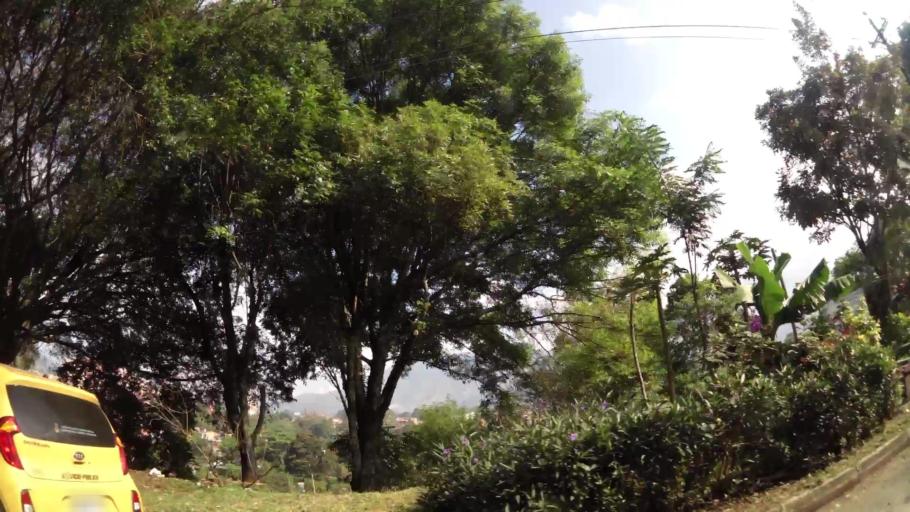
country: CO
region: Antioquia
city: La Estrella
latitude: 6.1718
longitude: -75.6414
